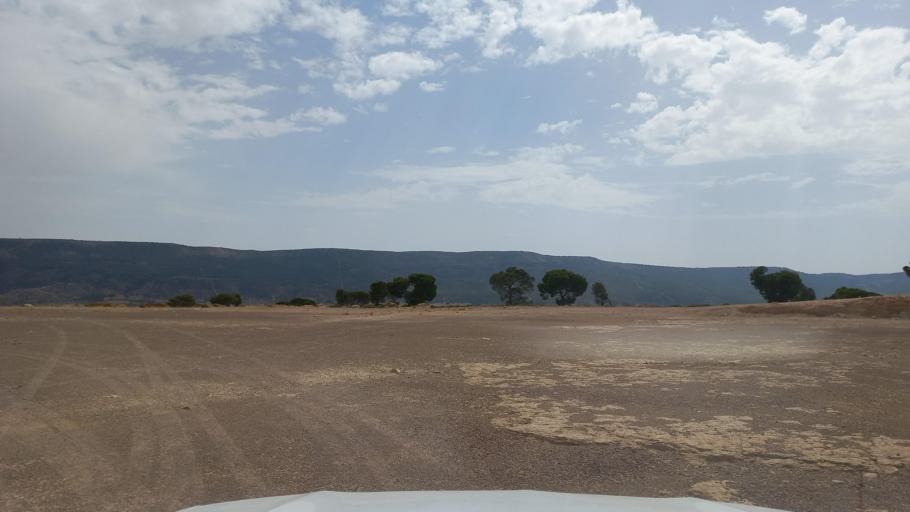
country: TN
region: Al Qasrayn
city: Kasserine
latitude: 35.3769
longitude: 8.8786
